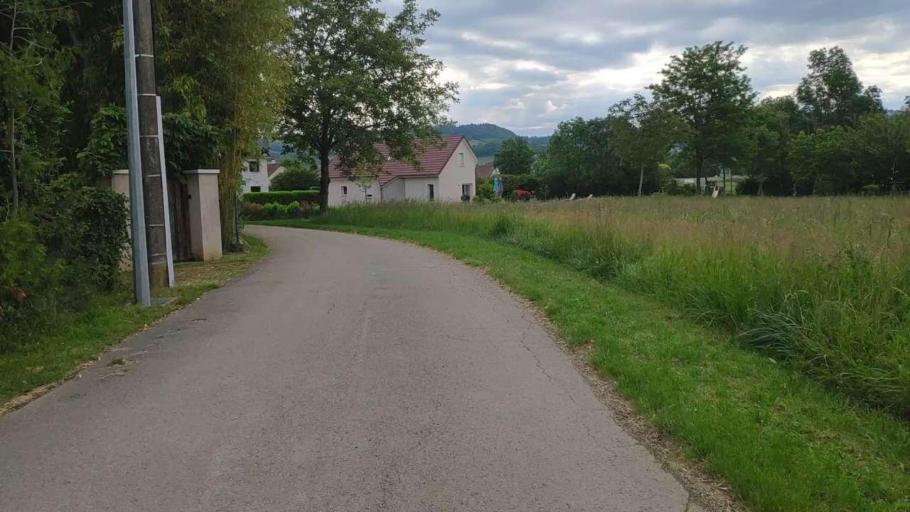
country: FR
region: Franche-Comte
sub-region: Departement du Jura
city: Perrigny
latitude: 46.7611
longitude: 5.5898
